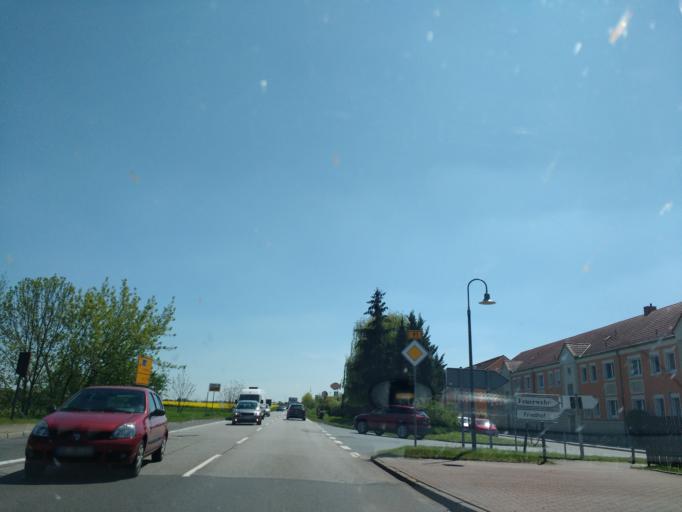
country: DE
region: Saxony-Anhalt
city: Theissen
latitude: 51.0840
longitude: 12.1102
